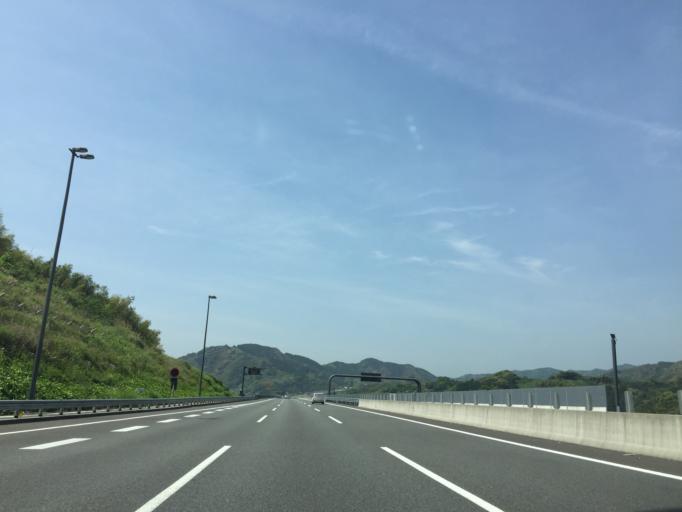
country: JP
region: Shizuoka
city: Fujieda
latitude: 34.9092
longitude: 138.2531
